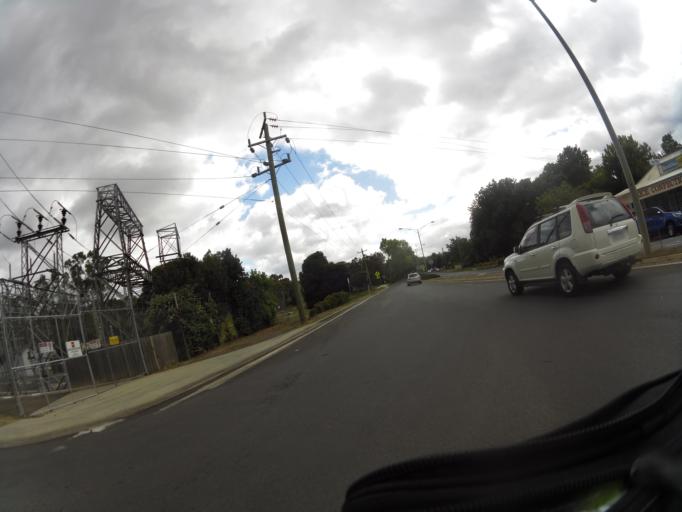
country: AU
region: Victoria
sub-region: Mount Alexander
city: Castlemaine
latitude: -37.0728
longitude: 144.2069
